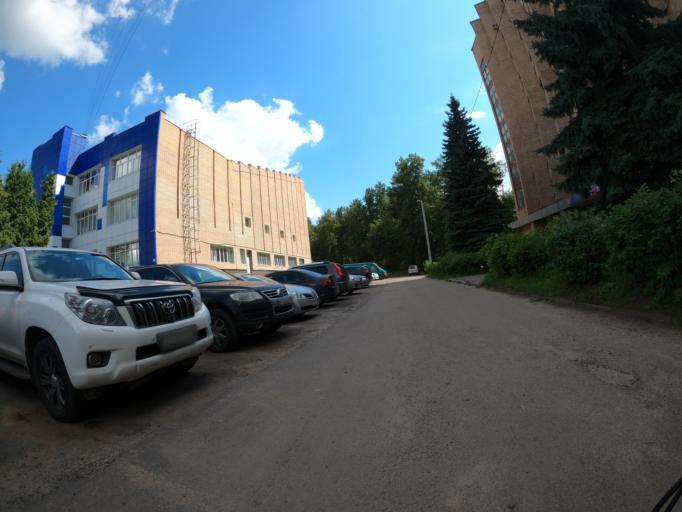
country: RU
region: Moskovskaya
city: Voskresensk
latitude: 55.3203
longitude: 38.6685
